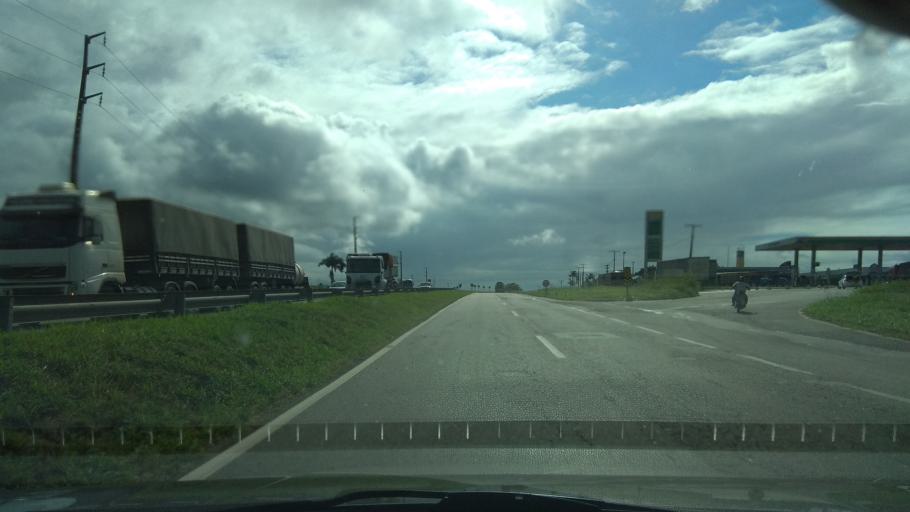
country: BR
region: Bahia
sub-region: Conceicao Do Jacuipe
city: Conceicao do Jacuipe
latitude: -12.3410
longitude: -38.8448
